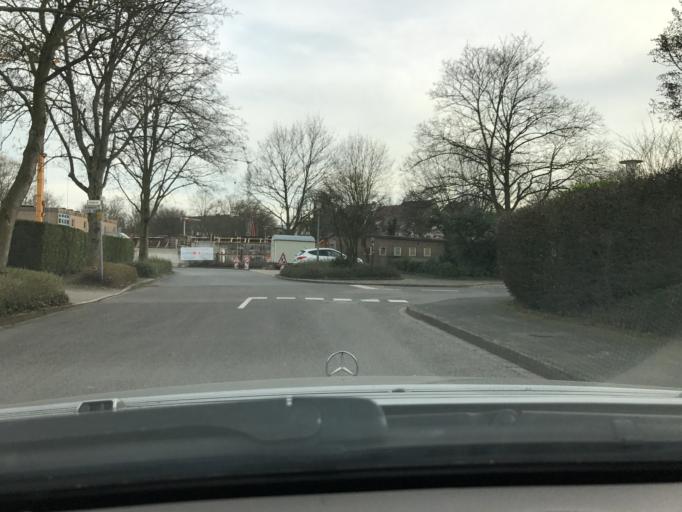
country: DE
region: North Rhine-Westphalia
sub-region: Regierungsbezirk Dusseldorf
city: Krefeld
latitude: 51.3427
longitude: 6.5738
